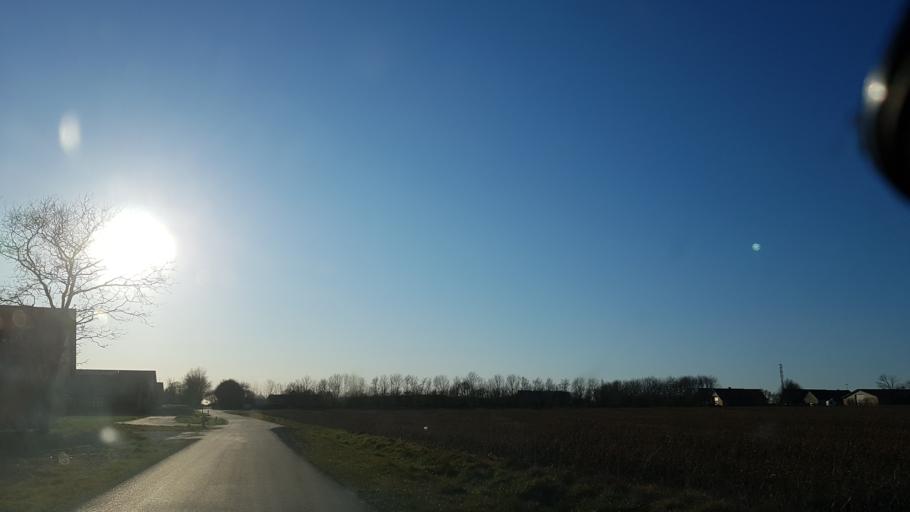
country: DK
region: South Denmark
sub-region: Esbjerg Kommune
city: Bramming
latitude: 55.4219
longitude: 8.6634
